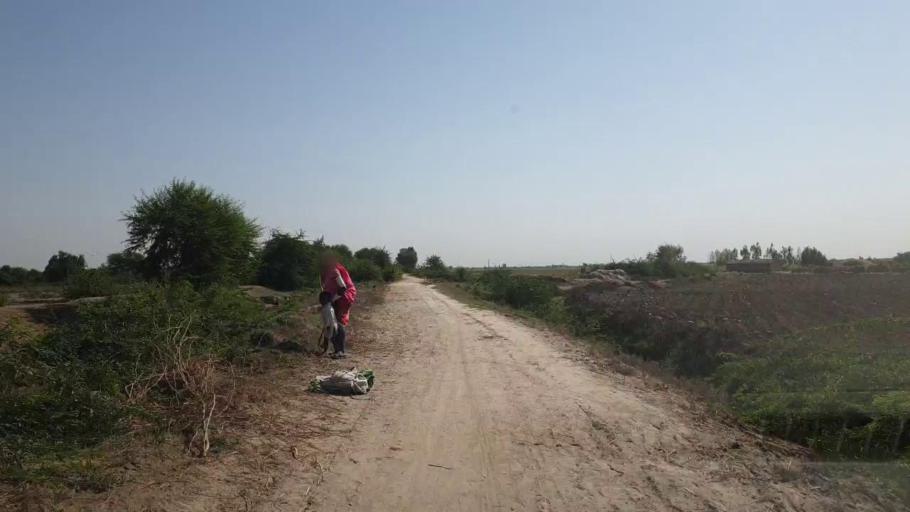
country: PK
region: Sindh
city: Kadhan
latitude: 24.6113
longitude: 68.9992
